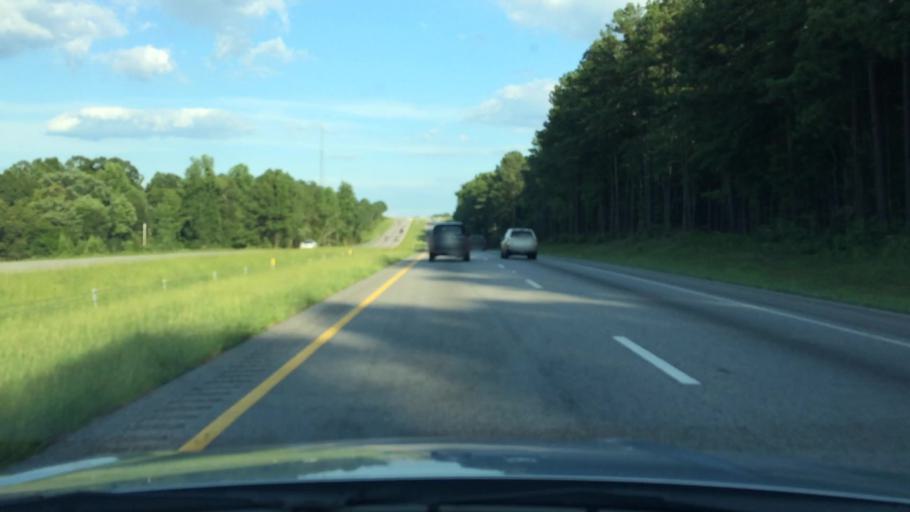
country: US
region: South Carolina
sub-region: Laurens County
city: Joanna
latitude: 34.4447
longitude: -81.7706
